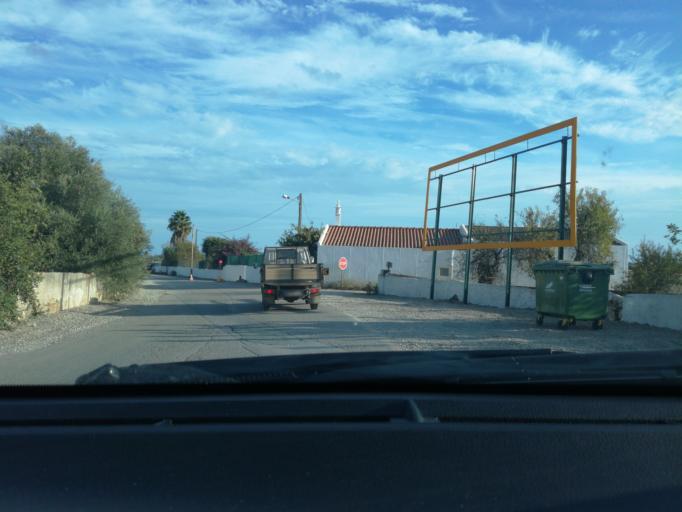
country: PT
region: Faro
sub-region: Olhao
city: Moncarapacho
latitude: 37.0796
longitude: -7.7805
